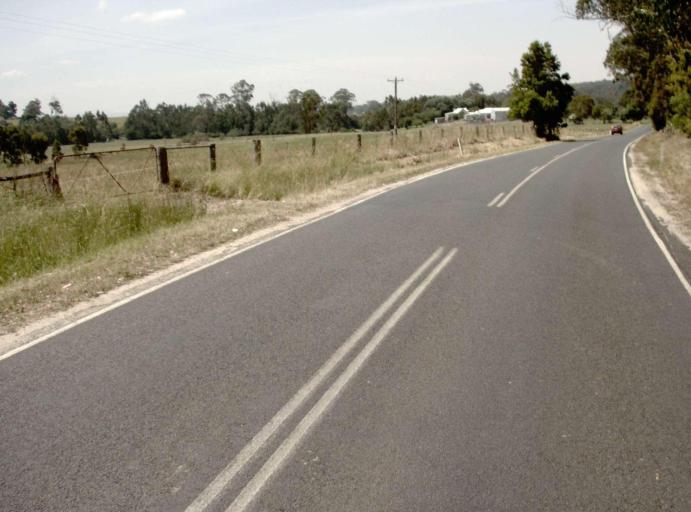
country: AU
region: Victoria
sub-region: Latrobe
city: Traralgon
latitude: -38.2895
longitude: 146.5399
